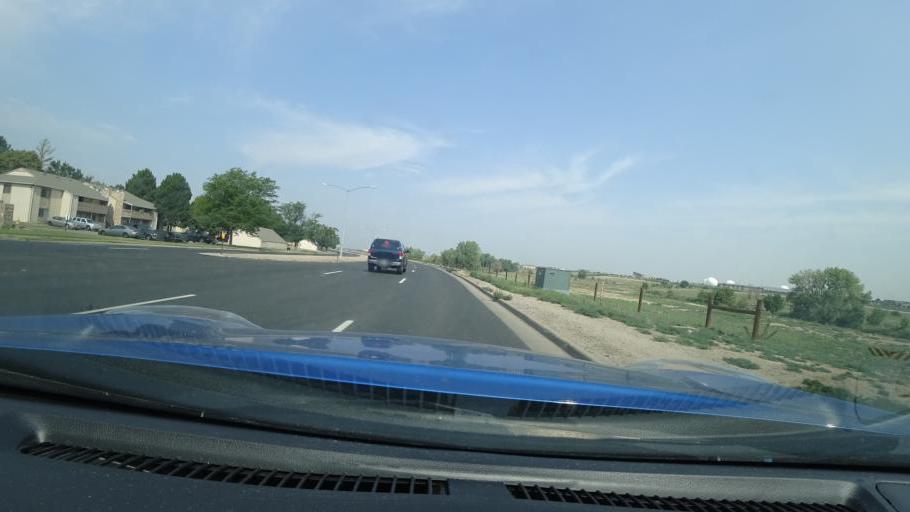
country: US
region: Colorado
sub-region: Adams County
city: Aurora
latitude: 39.7037
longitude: -104.7761
